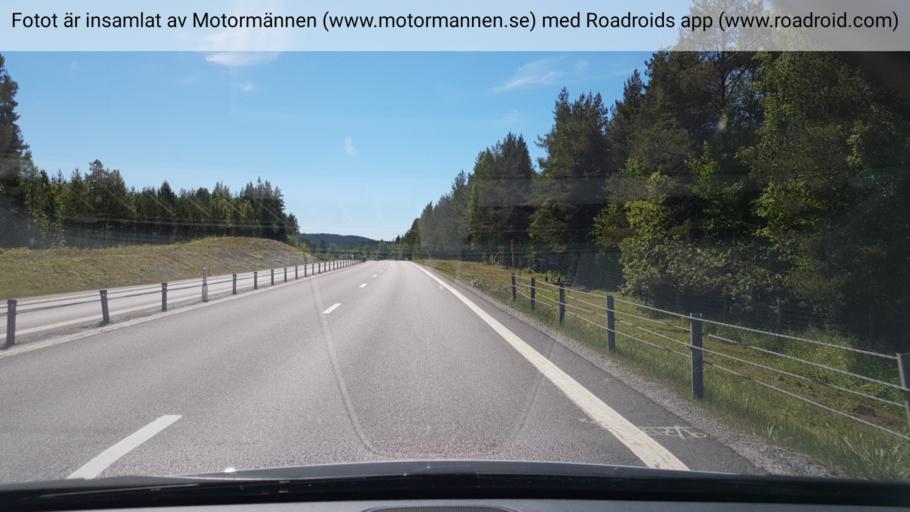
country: SE
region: Norrbotten
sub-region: Pitea Kommun
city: Pitea
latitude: 65.1655
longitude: 21.4934
